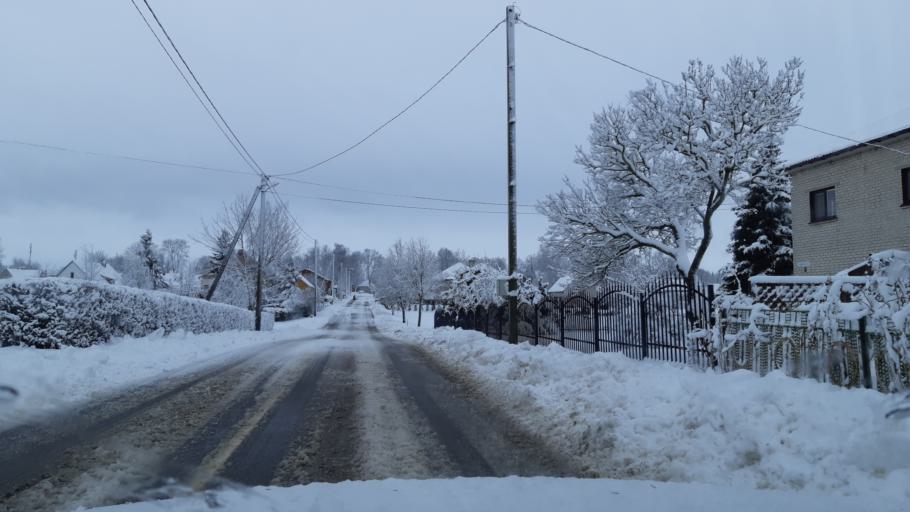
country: LT
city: Virbalis
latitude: 54.6291
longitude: 22.8244
